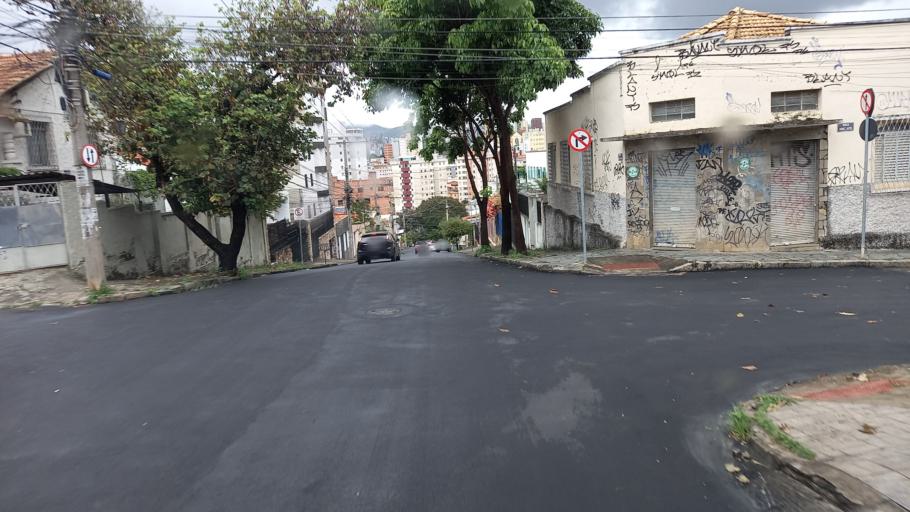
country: BR
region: Minas Gerais
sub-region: Belo Horizonte
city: Belo Horizonte
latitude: -19.9075
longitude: -43.9263
